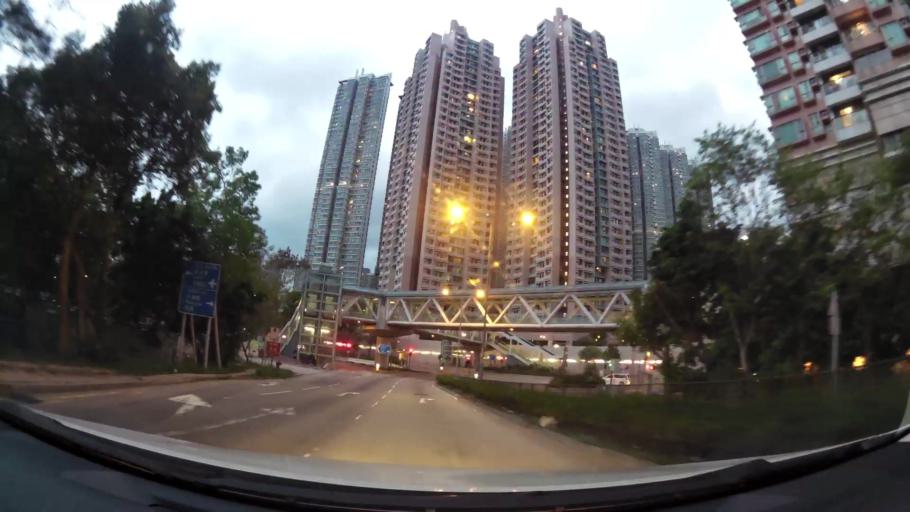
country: HK
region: Sham Shui Po
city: Sham Shui Po
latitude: 22.3228
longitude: 114.1590
